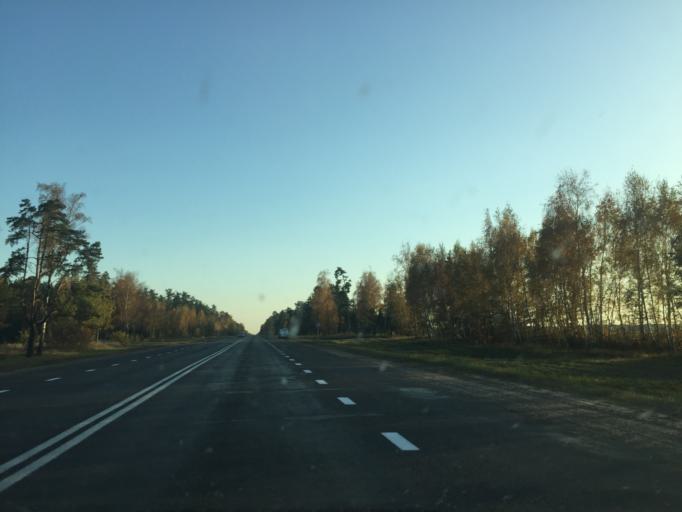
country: BY
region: Mogilev
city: Poselok Voskhod
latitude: 53.7325
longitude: 30.3666
